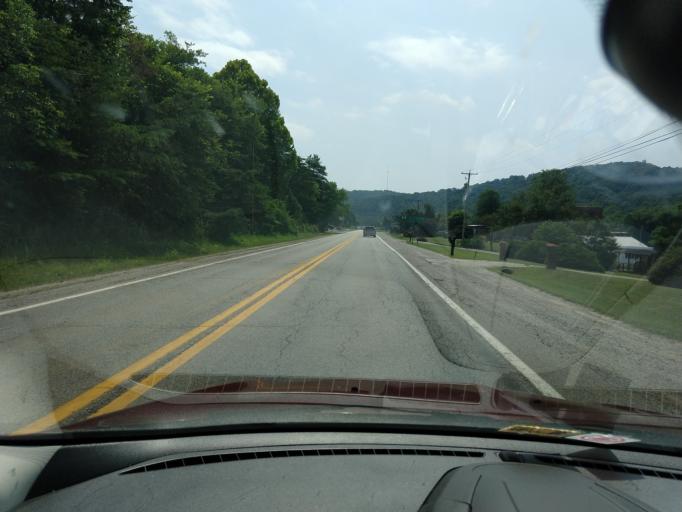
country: US
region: West Virginia
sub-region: Jackson County
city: Ripley
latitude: 38.8205
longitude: -81.7403
